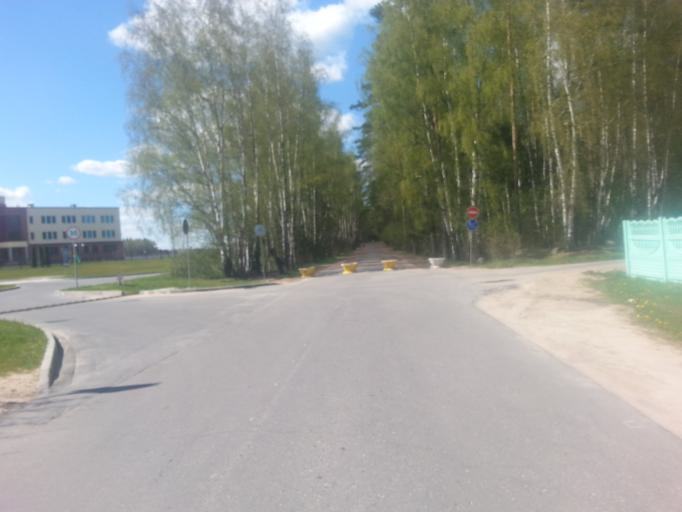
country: BY
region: Minsk
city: Narach
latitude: 54.9184
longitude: 26.6986
